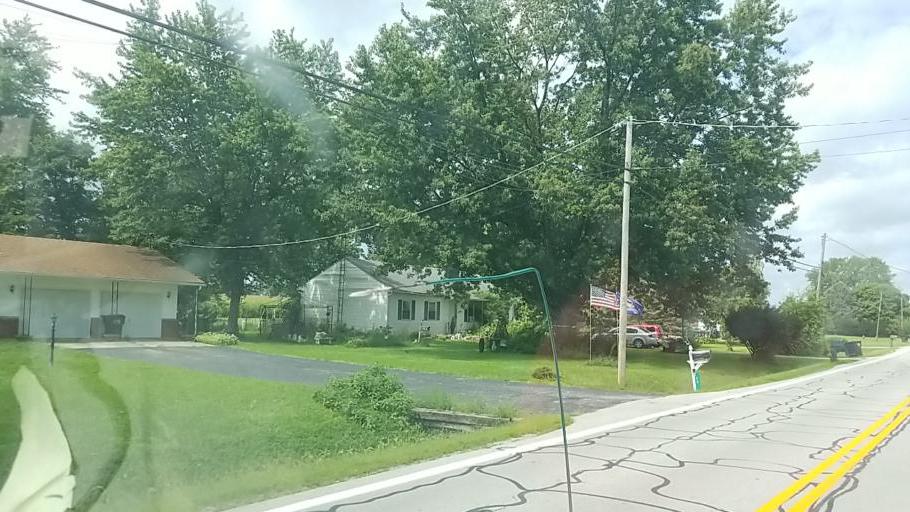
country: US
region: Ohio
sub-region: Fayette County
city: Jeffersonville
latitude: 39.6591
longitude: -83.5688
